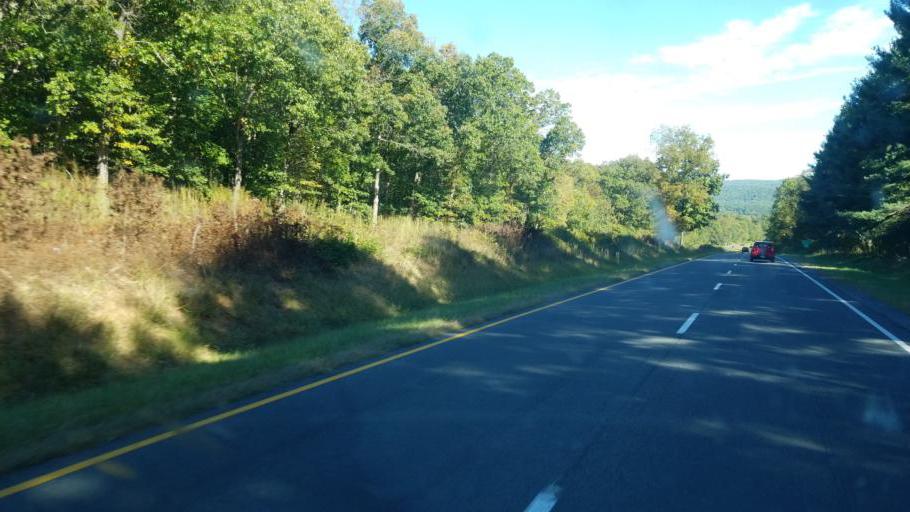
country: US
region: Virginia
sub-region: Warren County
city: Shenandoah Farms
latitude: 39.0482
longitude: -78.0124
